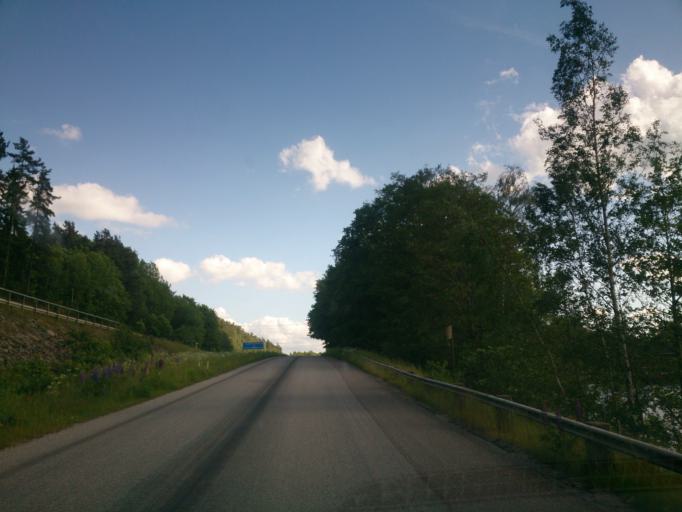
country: SE
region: OEstergoetland
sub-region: Norrkopings Kommun
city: Jursla
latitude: 58.6987
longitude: 16.1558
